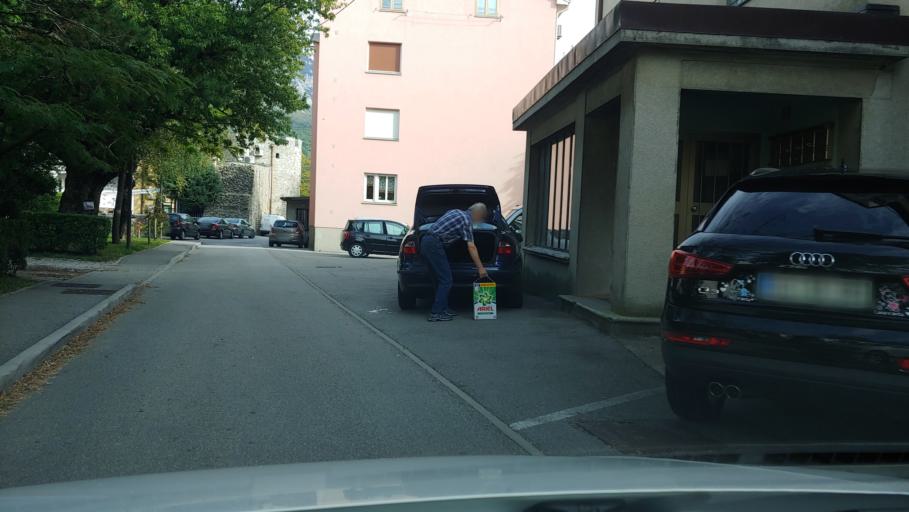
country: SI
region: Ajdovscina
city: Ajdovscina
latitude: 45.8878
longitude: 13.9034
